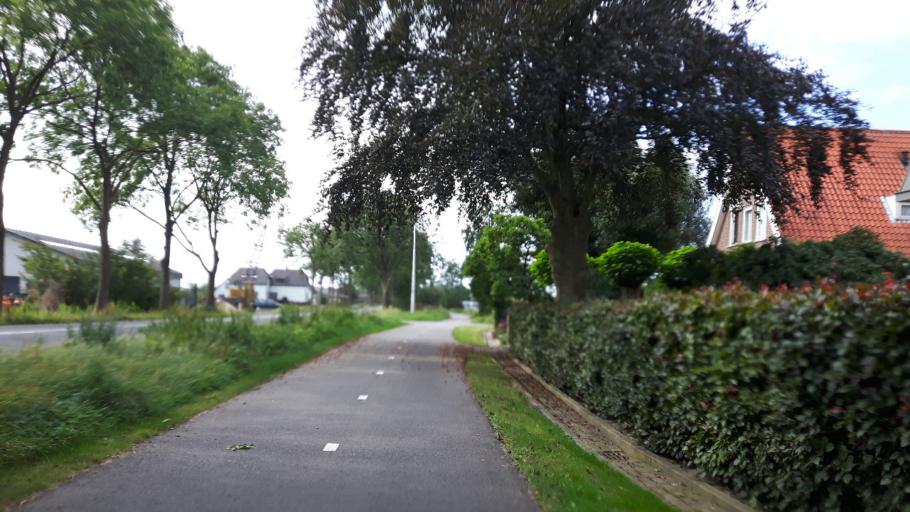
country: NL
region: Utrecht
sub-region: Gemeente De Ronde Venen
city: Mijdrecht
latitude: 52.1597
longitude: 4.8851
